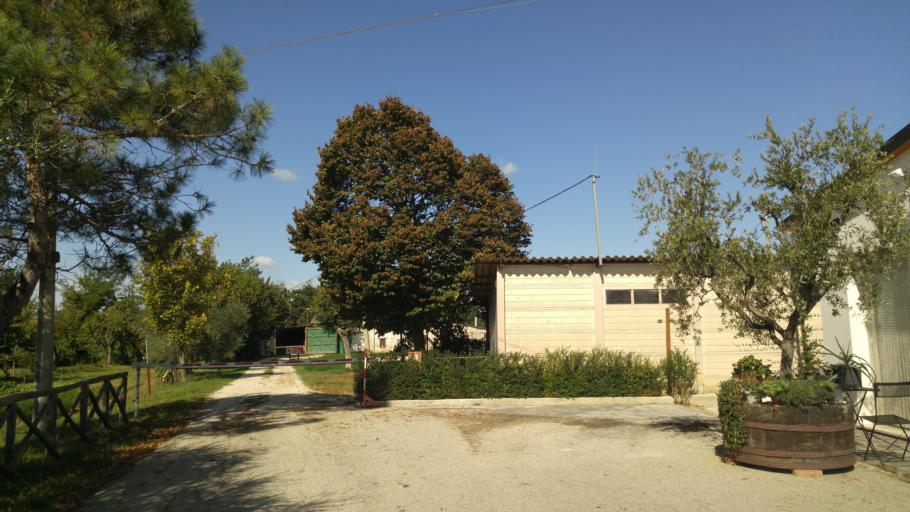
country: IT
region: The Marches
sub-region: Provincia di Pesaro e Urbino
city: Cuccurano
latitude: 43.7788
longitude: 12.9558
